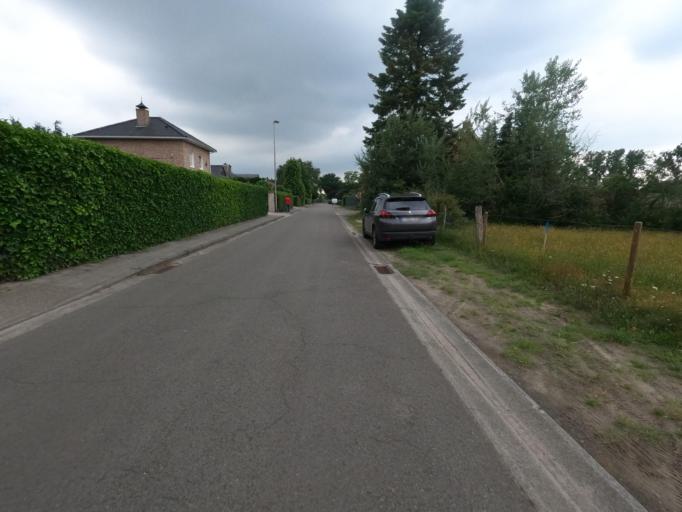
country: BE
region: Flanders
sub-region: Provincie Antwerpen
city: Essen
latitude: 51.4712
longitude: 4.4967
